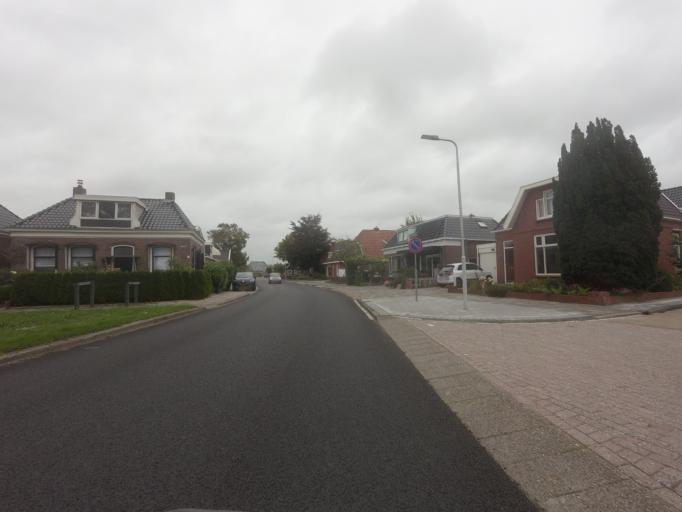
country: NL
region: Friesland
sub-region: Gemeente Leeuwarderadeel
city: Stiens
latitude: 53.2578
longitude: 5.7610
